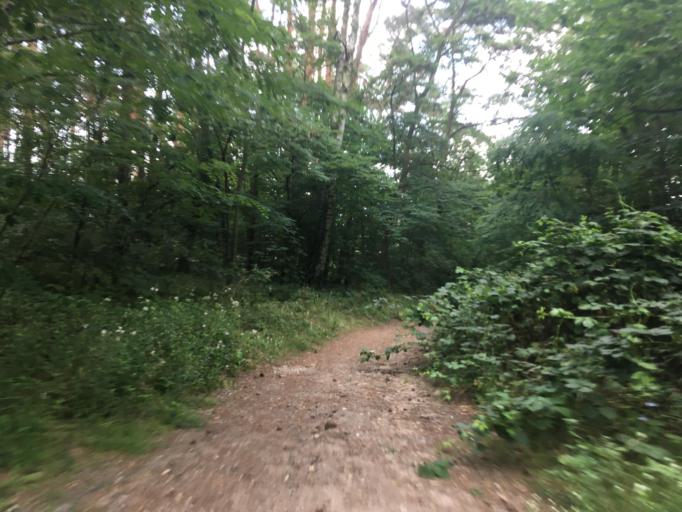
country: DE
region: Brandenburg
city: Wildau
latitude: 52.3315
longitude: 13.6228
